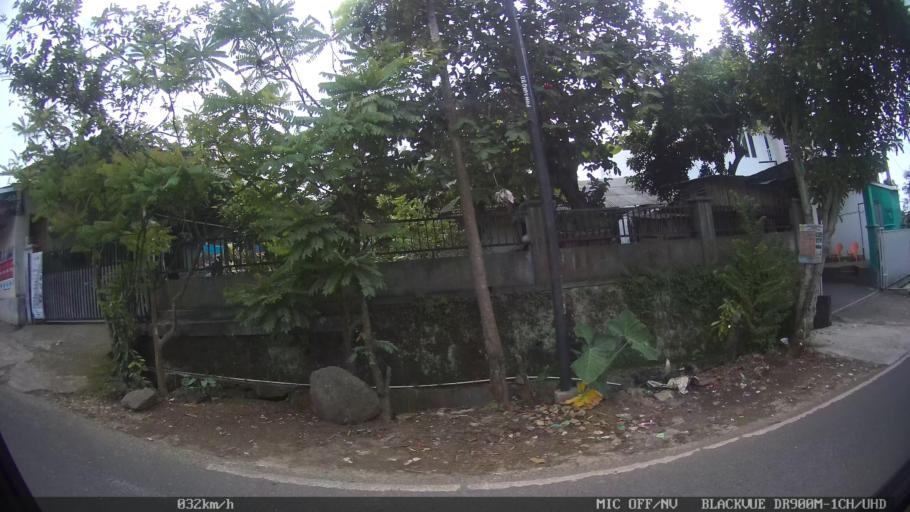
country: ID
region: Lampung
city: Bandarlampung
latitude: -5.4416
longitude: 105.2398
